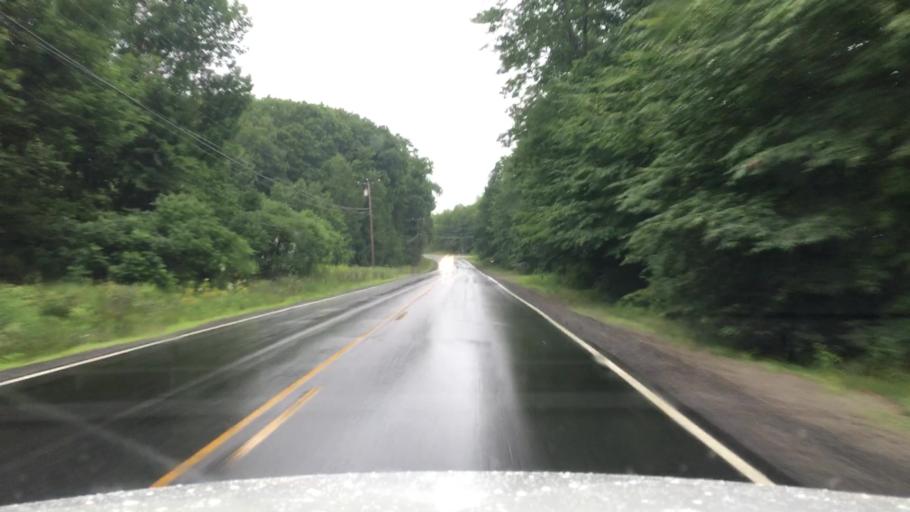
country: US
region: Maine
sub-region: Kennebec County
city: Manchester
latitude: 44.3125
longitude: -69.8370
